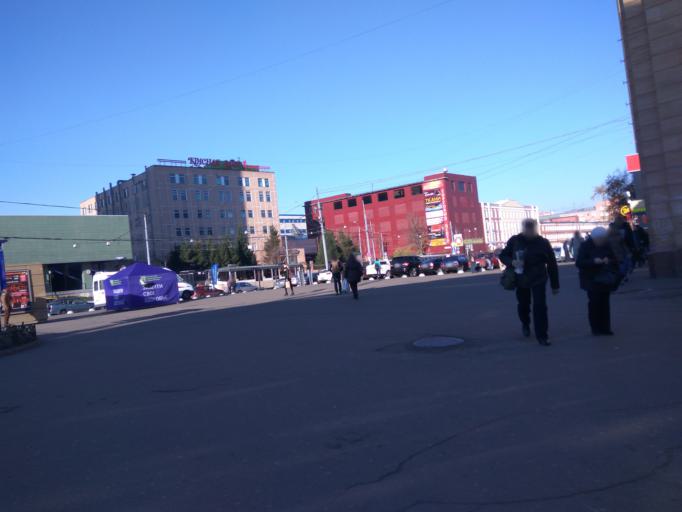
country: RU
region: Moscow
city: Lefortovo
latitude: 55.7829
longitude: 37.7193
